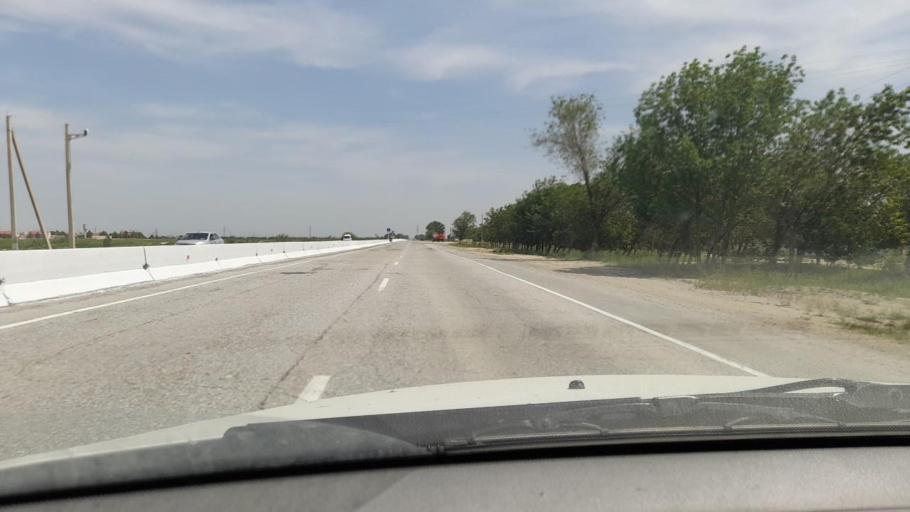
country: UZ
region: Navoiy
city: Konimex
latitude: 40.1118
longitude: 65.0760
